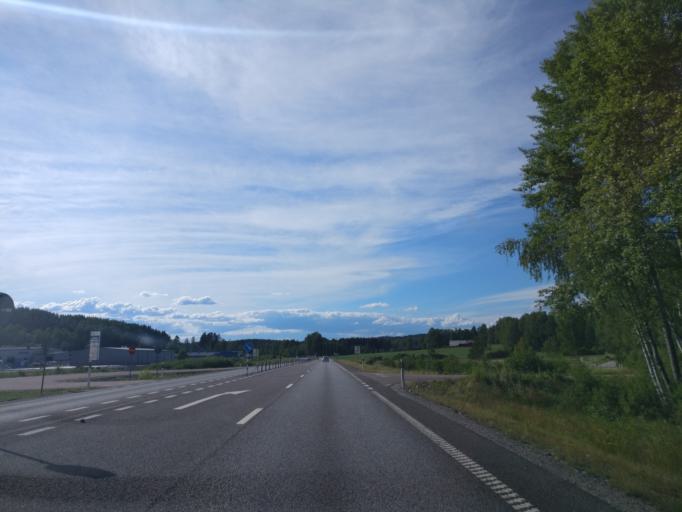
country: SE
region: Vaermland
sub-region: Arvika Kommun
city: Arvika
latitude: 59.6577
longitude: 12.6449
